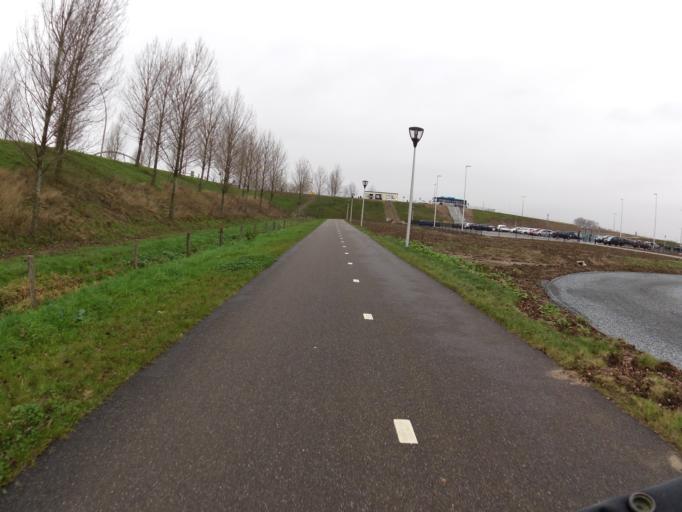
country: NL
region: Gelderland
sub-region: Gemeente Overbetuwe
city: Oosterhout
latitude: 51.8812
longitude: 5.8599
